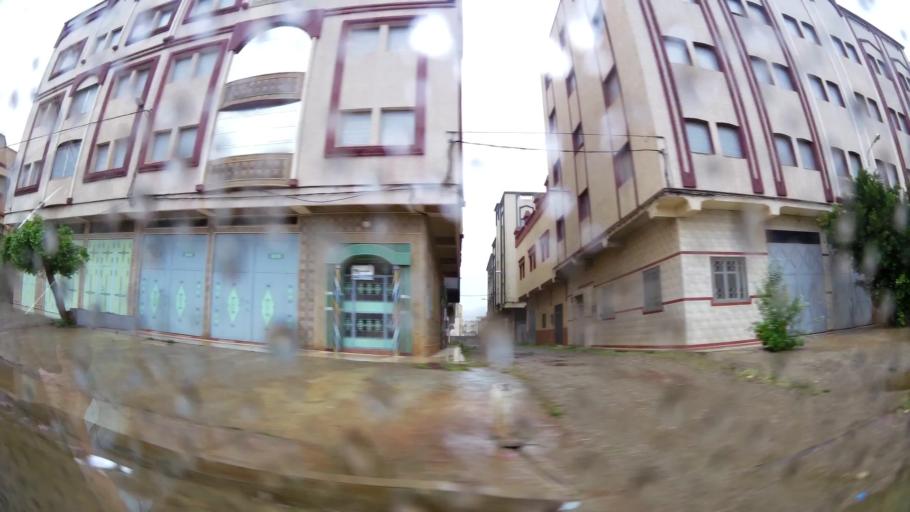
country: MA
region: Oriental
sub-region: Nador
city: Boudinar
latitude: 35.1182
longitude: -3.6438
